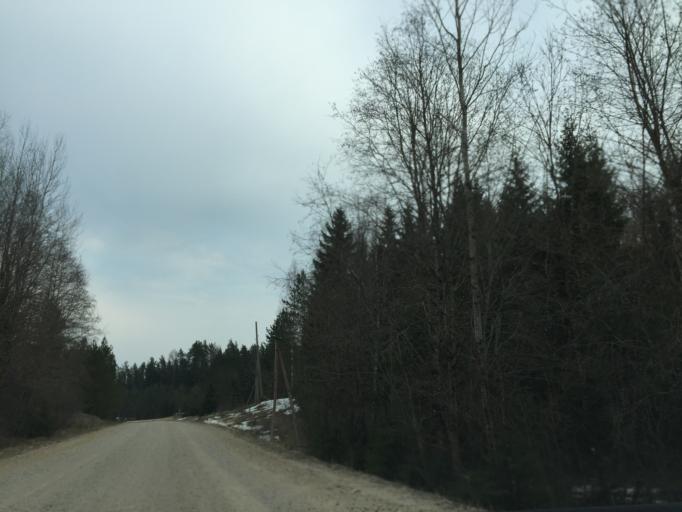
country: LV
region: Raunas
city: Rauna
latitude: 57.1622
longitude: 25.5233
